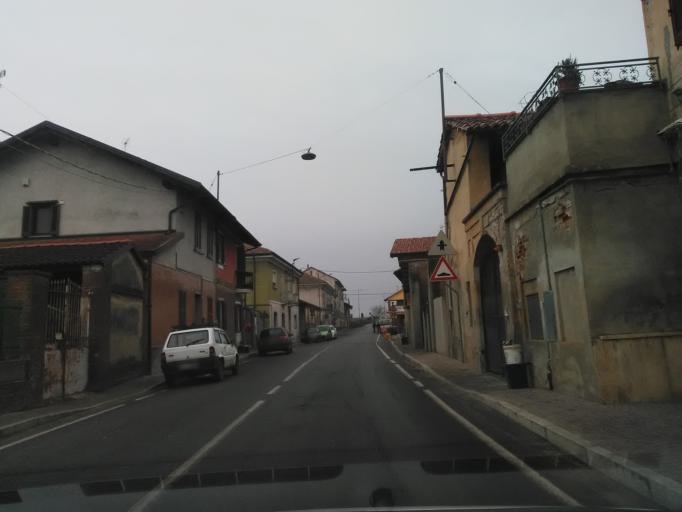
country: IT
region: Piedmont
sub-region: Provincia di Vercelli
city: Crova
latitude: 45.3308
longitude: 8.2096
